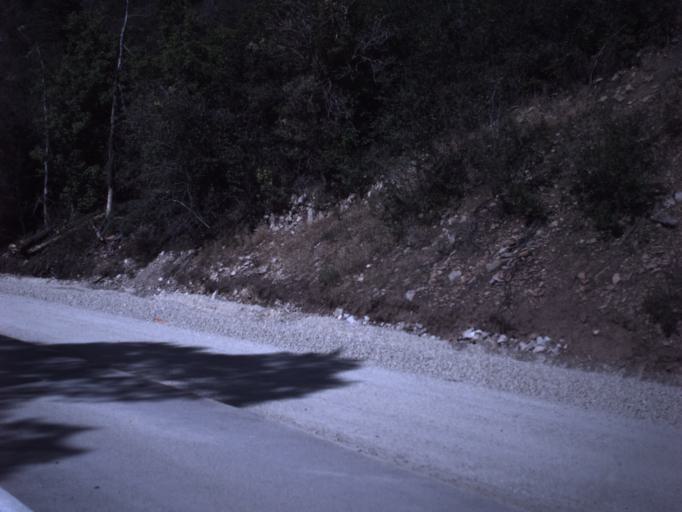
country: US
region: Utah
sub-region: Wasatch County
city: Heber
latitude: 40.3941
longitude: -111.3022
